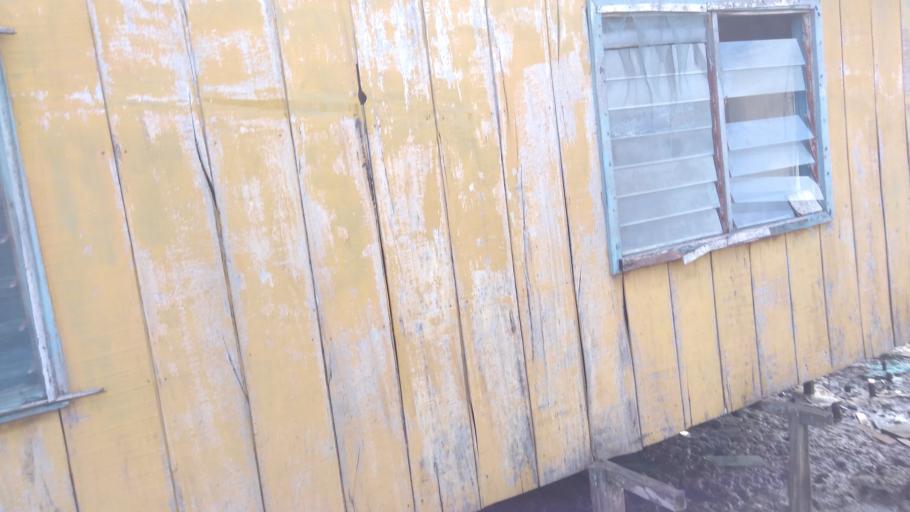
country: NG
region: Ondo
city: Igbekebo
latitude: 5.9240
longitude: 4.9647
